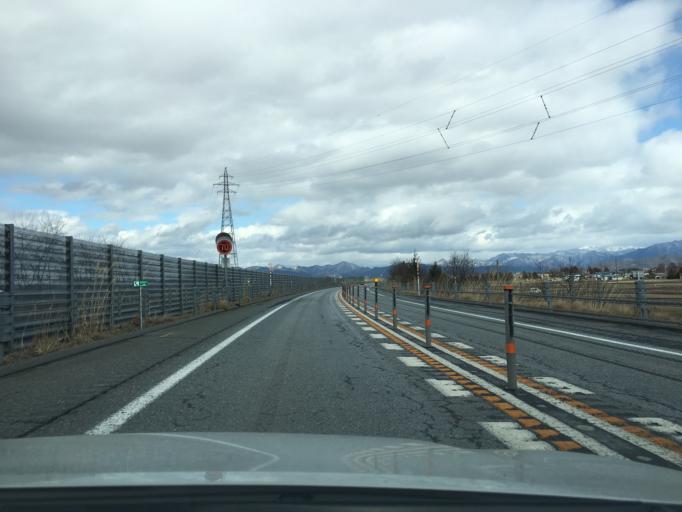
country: JP
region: Yamagata
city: Yonezawa
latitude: 37.9674
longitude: 140.1234
